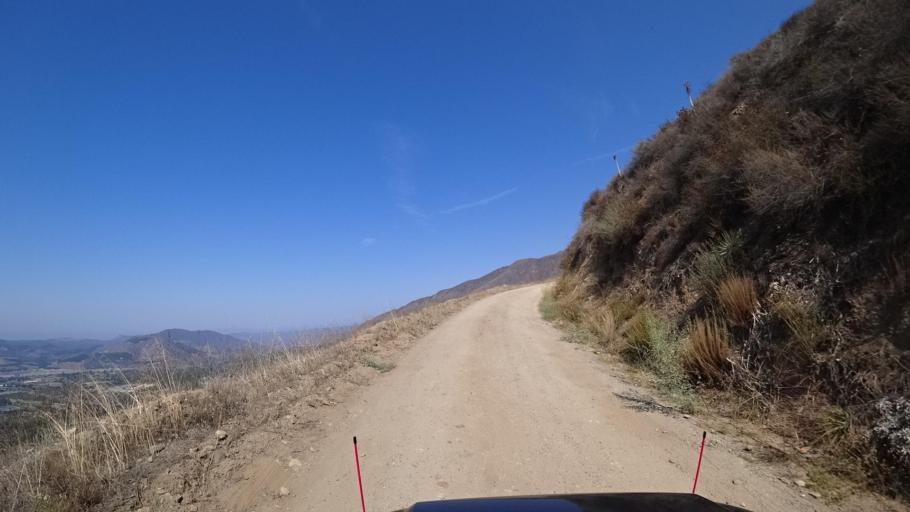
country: US
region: California
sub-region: San Diego County
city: Valley Center
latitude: 33.3274
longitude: -116.9634
